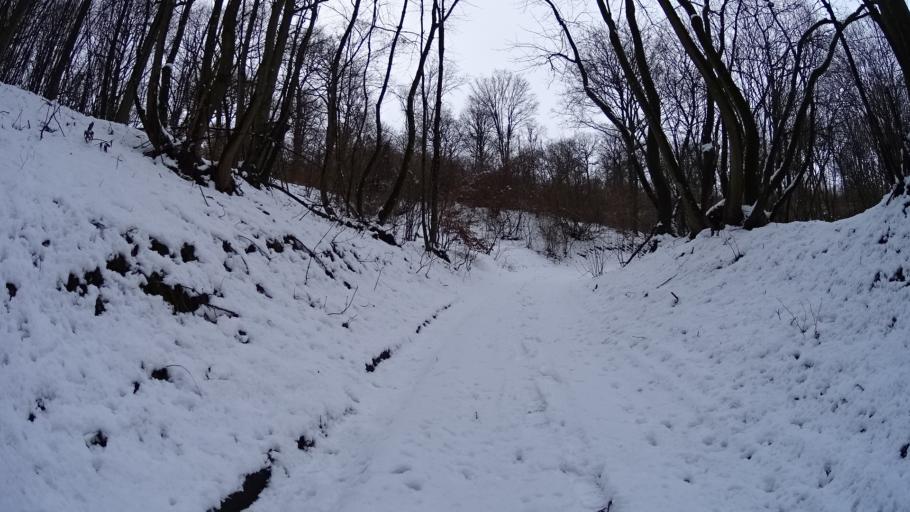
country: AT
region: Lower Austria
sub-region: Politischer Bezirk Korneuburg
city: Niederhollabrunn
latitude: 48.4190
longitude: 16.2904
